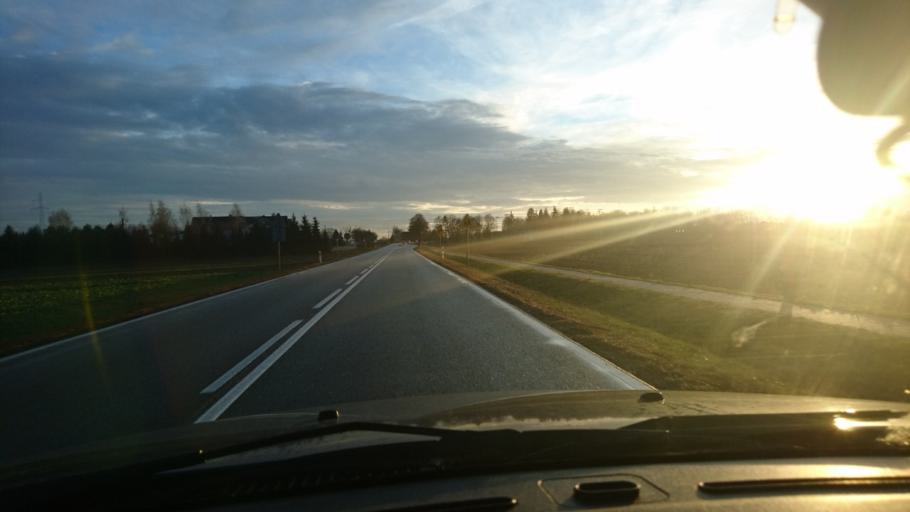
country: PL
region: Greater Poland Voivodeship
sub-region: Powiat kepinski
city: Opatow
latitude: 51.1860
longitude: 18.1468
